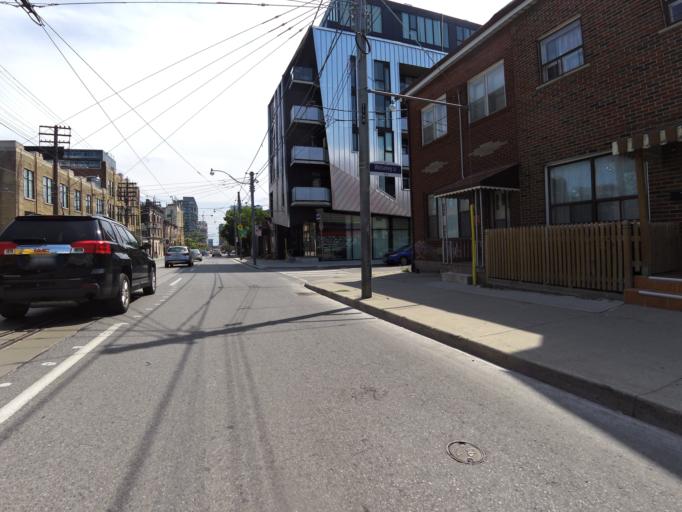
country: CA
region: Ontario
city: Toronto
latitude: 43.6483
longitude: -79.4045
